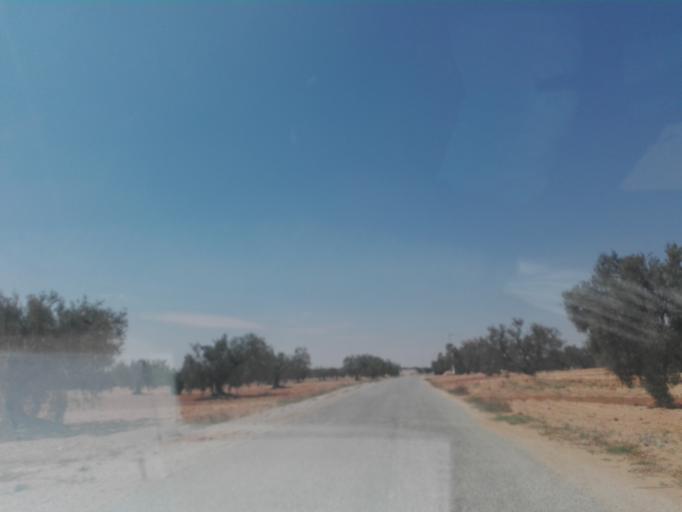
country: TN
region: Safaqis
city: Bi'r `Ali Bin Khalifah
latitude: 34.6253
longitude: 10.3702
